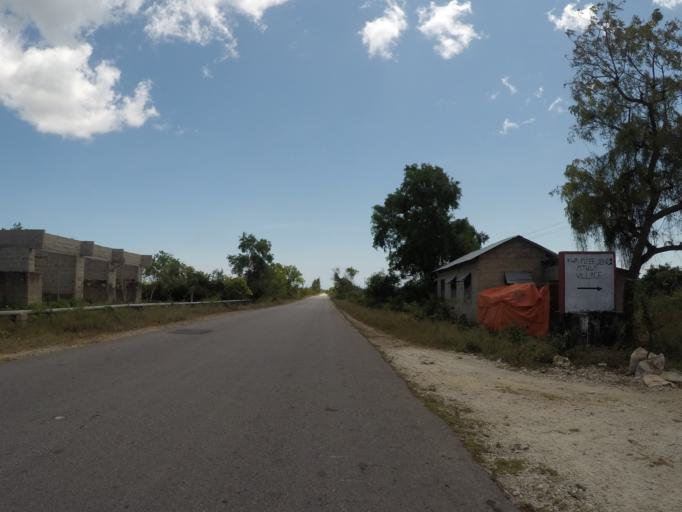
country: TZ
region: Zanzibar Central/South
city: Nganane
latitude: -6.2834
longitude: 39.4650
